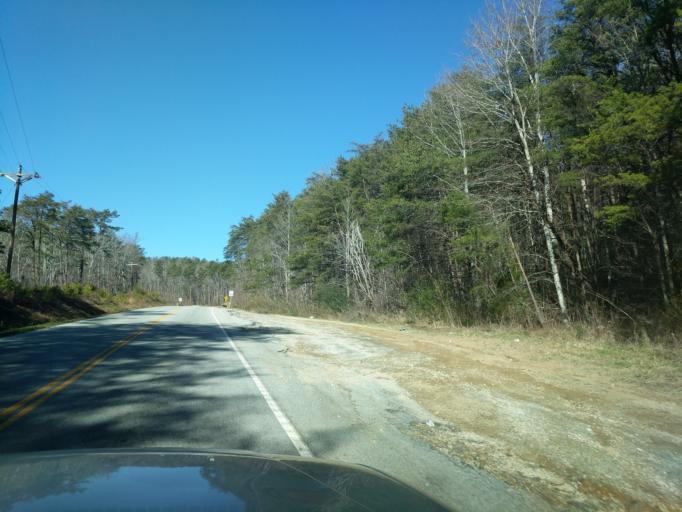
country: US
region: South Carolina
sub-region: Oconee County
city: Westminster
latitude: 34.7613
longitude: -83.2488
